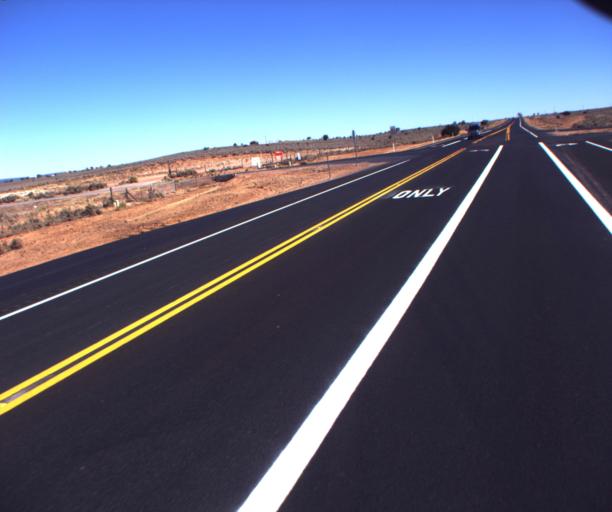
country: US
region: Arizona
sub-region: Apache County
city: Ganado
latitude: 35.7163
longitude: -109.4527
